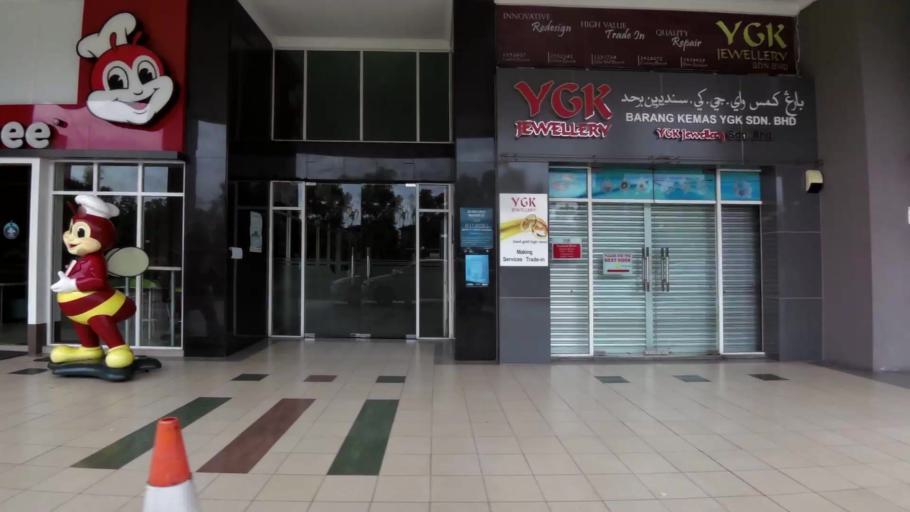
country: BN
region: Brunei and Muara
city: Bandar Seri Begawan
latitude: 4.9041
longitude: 114.9263
